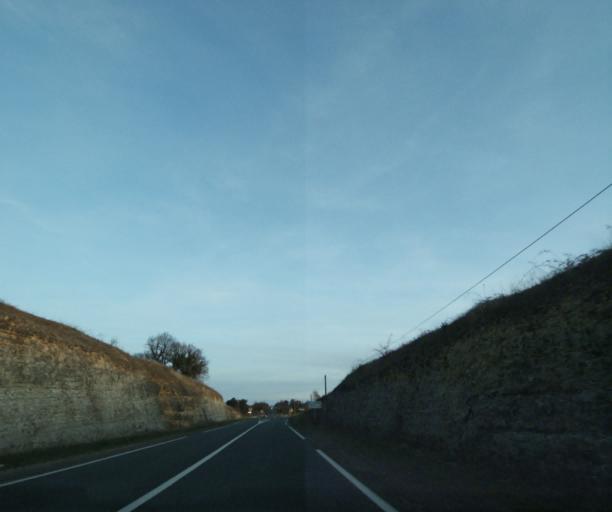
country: FR
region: Midi-Pyrenees
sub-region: Departement du Lot
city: Le Vigan
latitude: 44.6196
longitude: 1.4912
